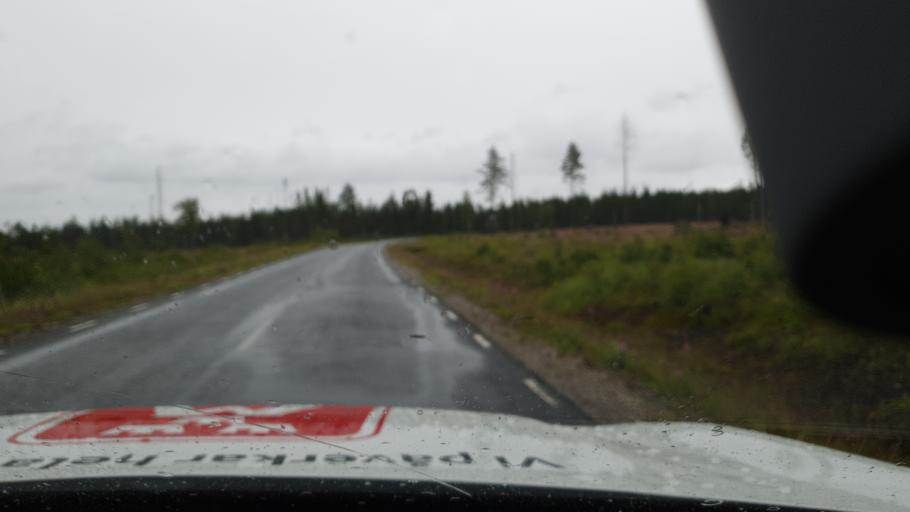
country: SE
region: Vaesterbotten
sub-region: Vindelns Kommun
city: Vindeln
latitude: 64.4718
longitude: 19.7619
